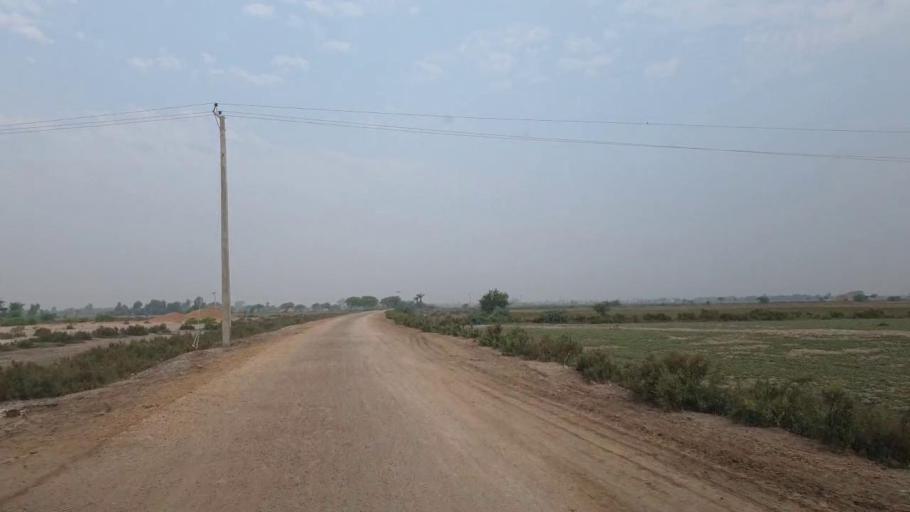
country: PK
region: Sindh
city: Tando Bago
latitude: 24.7816
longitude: 68.8888
